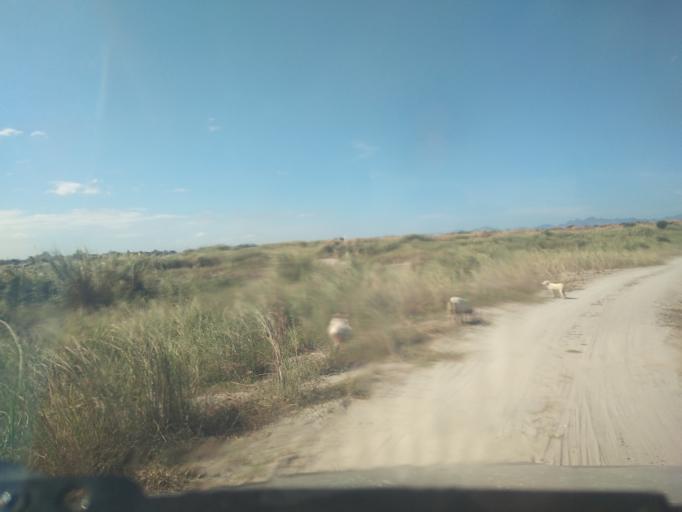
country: PH
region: Central Luzon
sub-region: Province of Pampanga
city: Calibutbut
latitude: 15.0825
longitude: 120.6061
